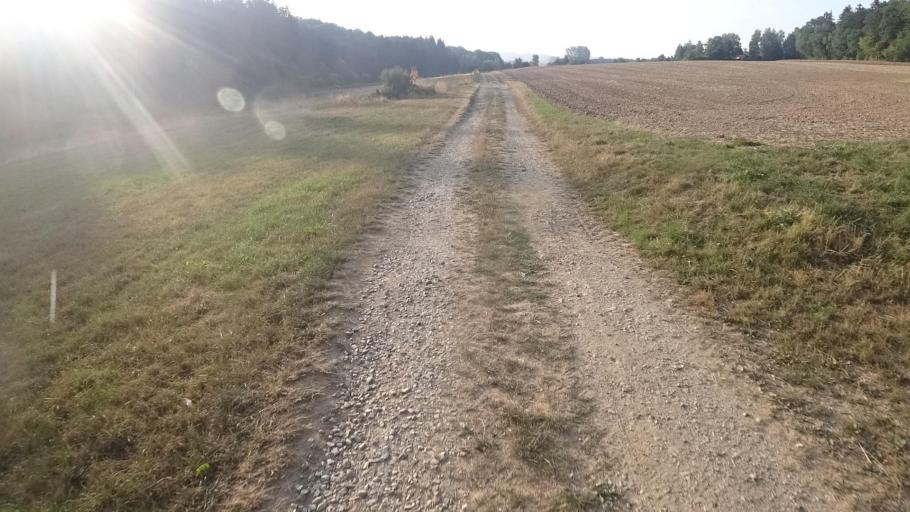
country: DE
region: Rheinland-Pfalz
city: Ohlweiler
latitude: 49.9600
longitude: 7.5168
